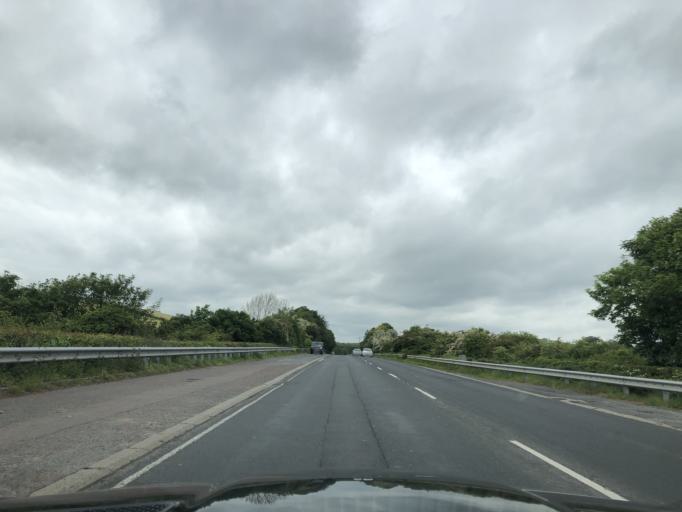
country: GB
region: Northern Ireland
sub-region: Down District
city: Downpatrick
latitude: 54.3371
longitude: -5.7236
